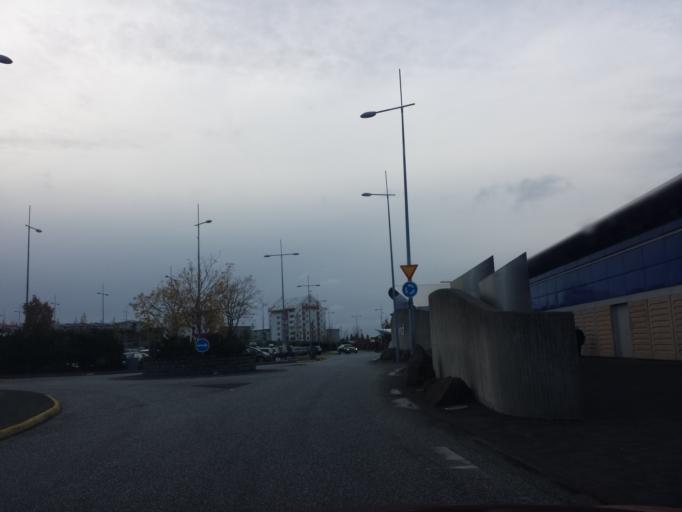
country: IS
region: Capital Region
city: Kopavogur
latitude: 64.1006
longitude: -21.8836
